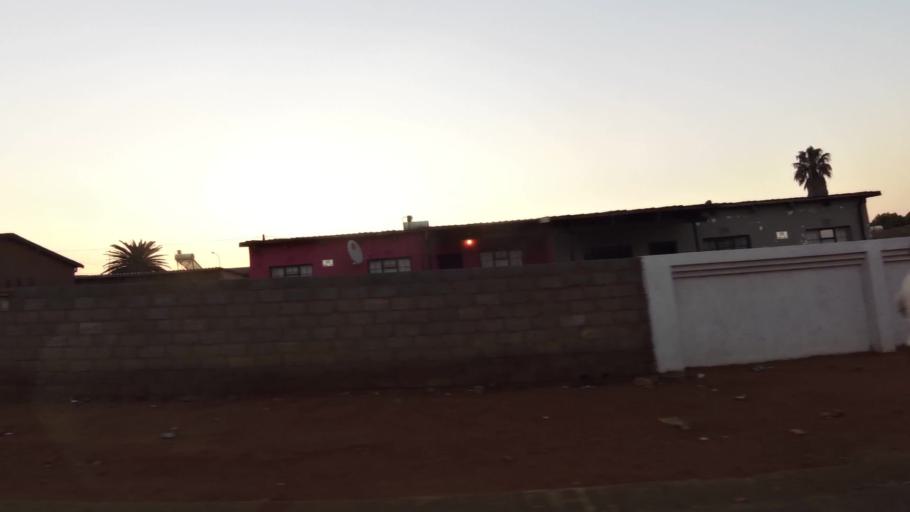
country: ZA
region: Gauteng
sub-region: City of Johannesburg Metropolitan Municipality
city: Soweto
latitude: -26.2853
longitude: 27.8780
